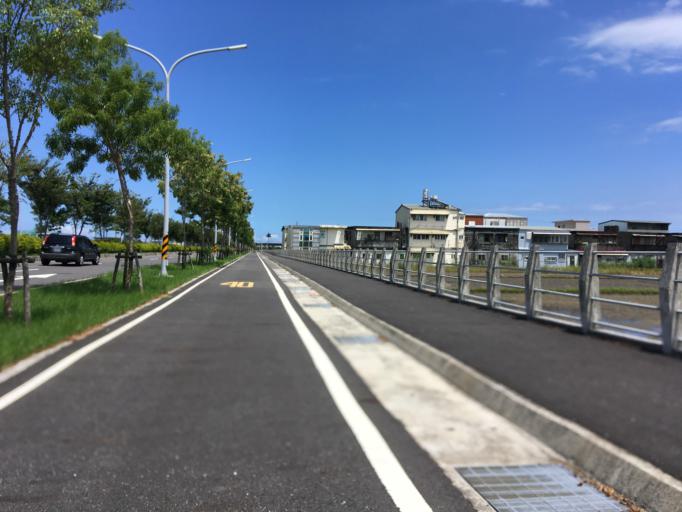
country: TW
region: Taiwan
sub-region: Yilan
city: Yilan
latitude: 24.6935
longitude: 121.7821
